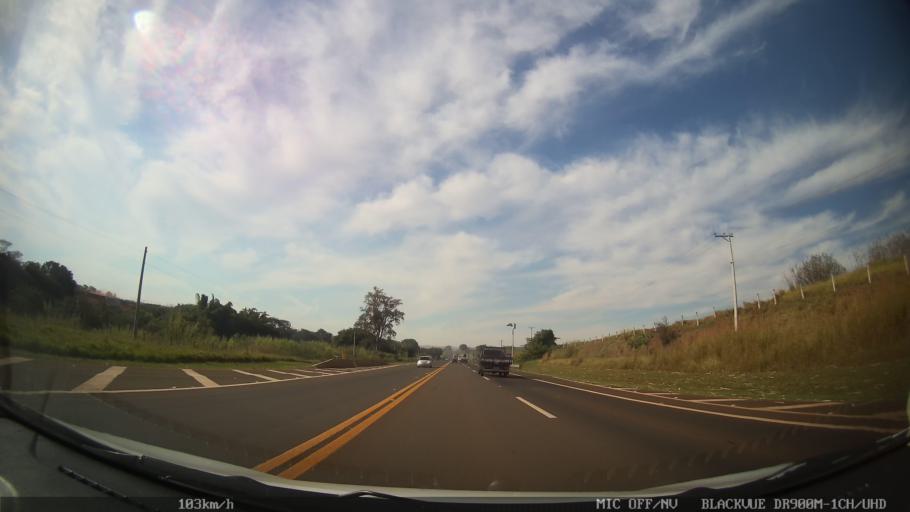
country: BR
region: Sao Paulo
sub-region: Araraquara
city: Araraquara
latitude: -21.7900
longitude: -48.1264
